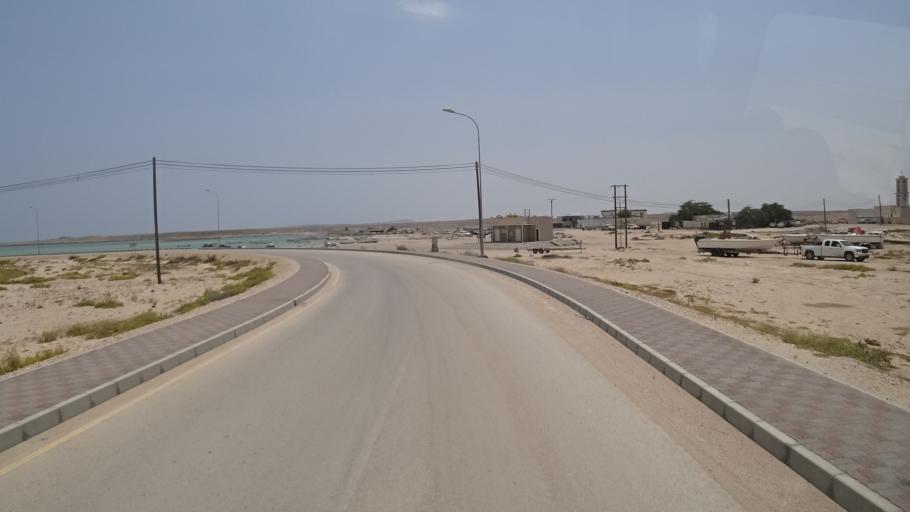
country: OM
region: Ash Sharqiyah
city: Sur
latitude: 22.5286
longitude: 59.7643
